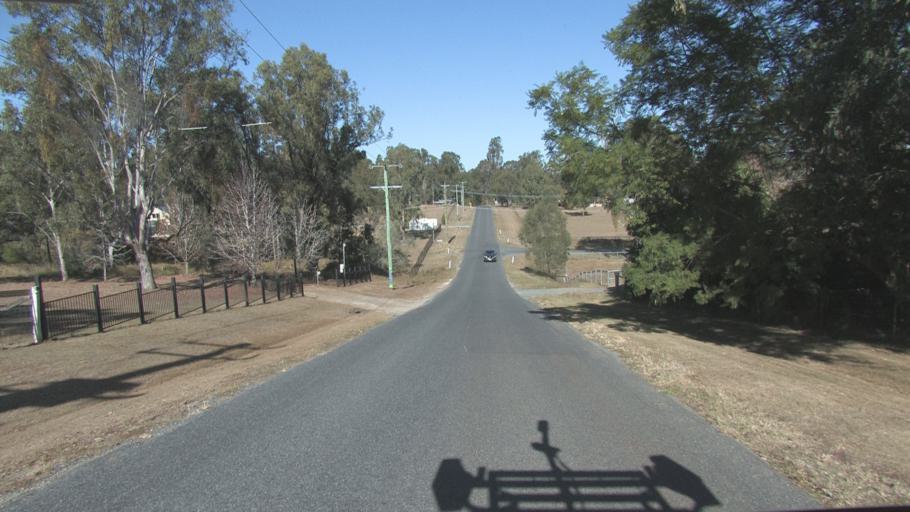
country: AU
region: Queensland
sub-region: Logan
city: Cedar Vale
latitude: -27.8666
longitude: 152.9843
